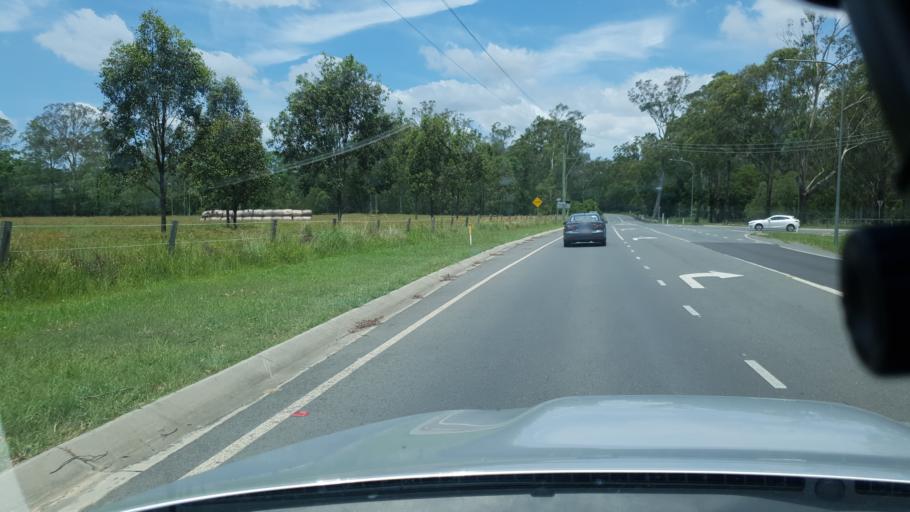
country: AU
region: Queensland
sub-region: Logan
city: North Maclean
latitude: -27.8280
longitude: 153.0141
